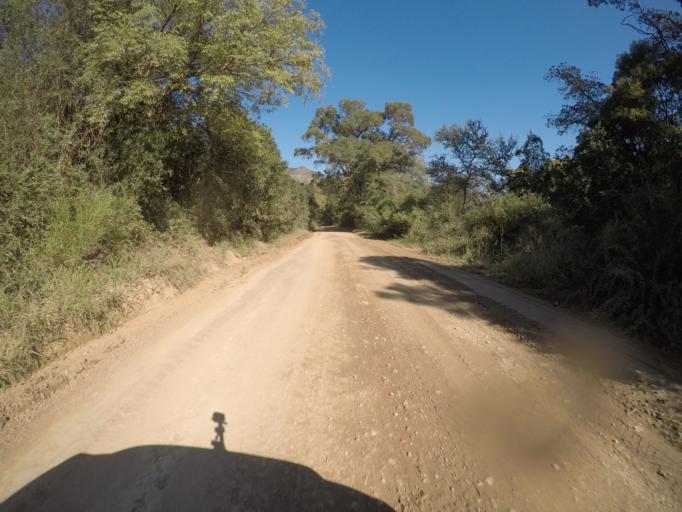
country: ZA
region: Eastern Cape
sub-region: Cacadu District Municipality
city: Kruisfontein
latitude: -33.6631
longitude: 24.5482
